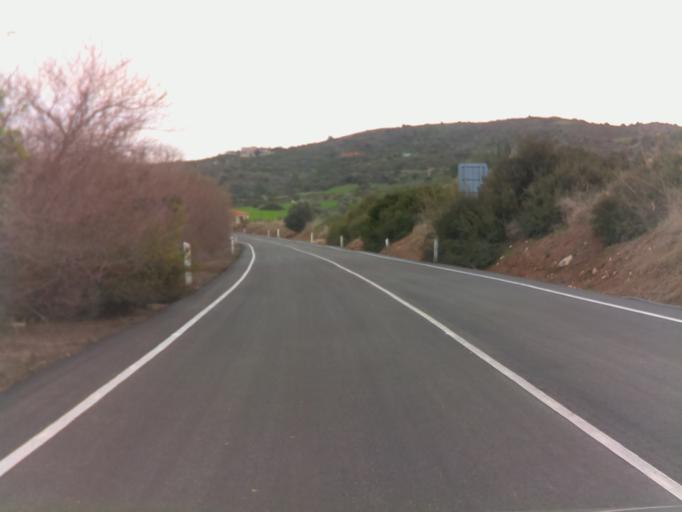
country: CY
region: Pafos
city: Polis
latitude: 35.0498
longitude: 32.3535
